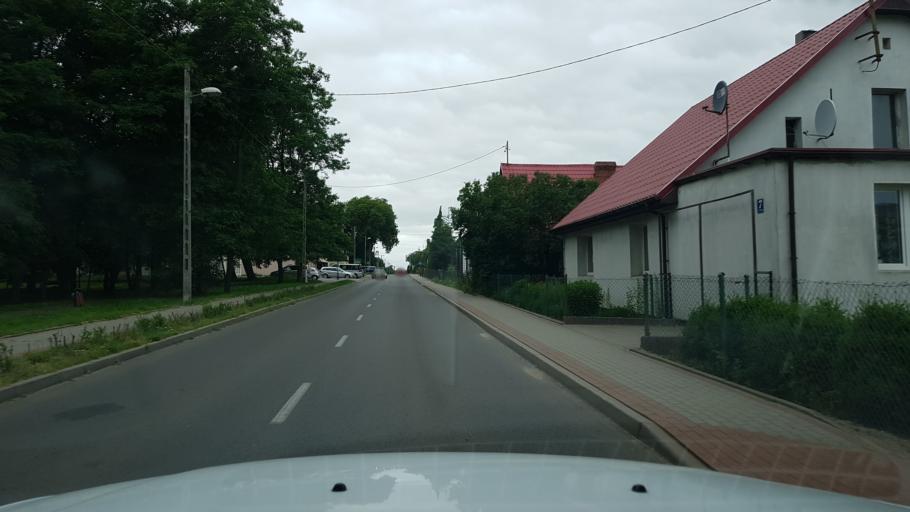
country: PL
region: West Pomeranian Voivodeship
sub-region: Powiat gryficki
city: Brojce
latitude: 53.9573
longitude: 15.3584
